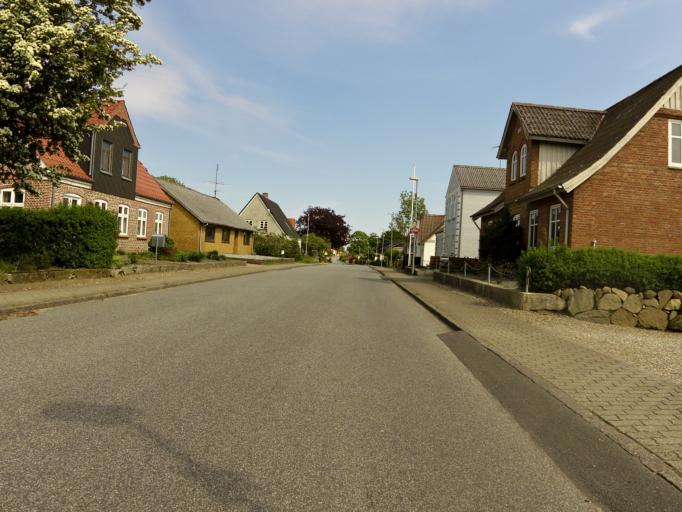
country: DK
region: South Denmark
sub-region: Haderslev Kommune
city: Gram
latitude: 55.2498
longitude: 8.9617
